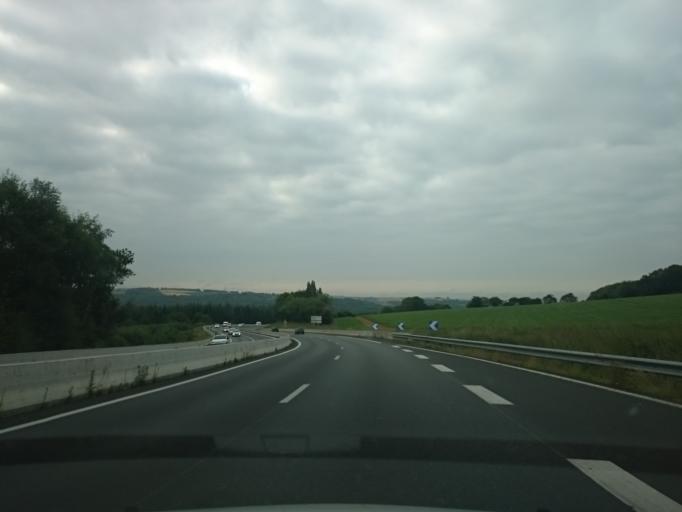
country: FR
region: Brittany
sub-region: Departement du Finistere
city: Daoulas
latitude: 48.3740
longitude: -4.2706
